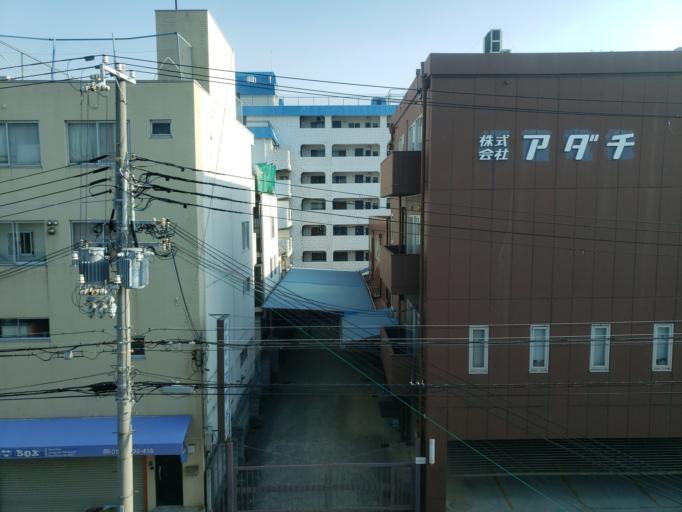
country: JP
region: Hyogo
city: Kobe
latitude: 34.6732
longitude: 135.1733
